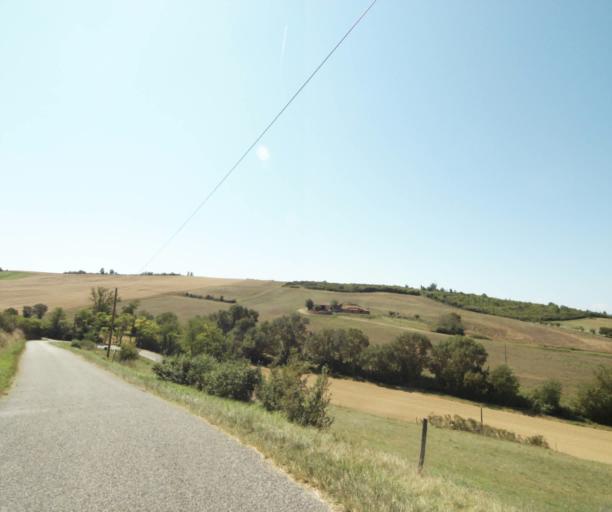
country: FR
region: Midi-Pyrenees
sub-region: Departement de l'Ariege
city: Lezat-sur-Leze
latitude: 43.2767
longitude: 1.3652
